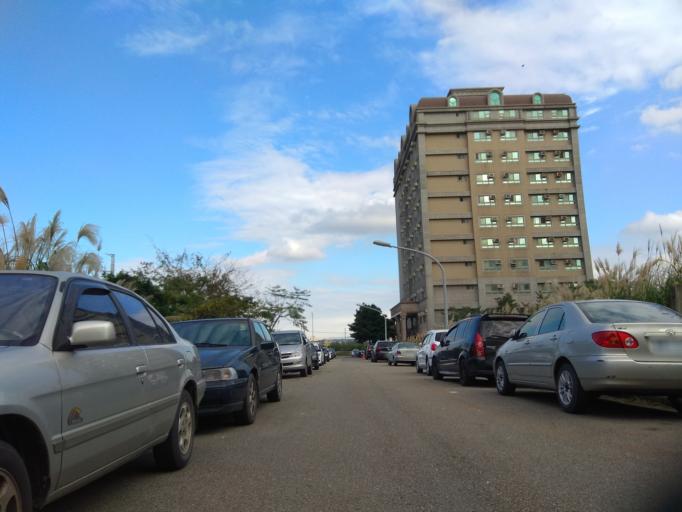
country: TW
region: Taiwan
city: Taoyuan City
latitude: 25.0617
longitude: 121.1766
